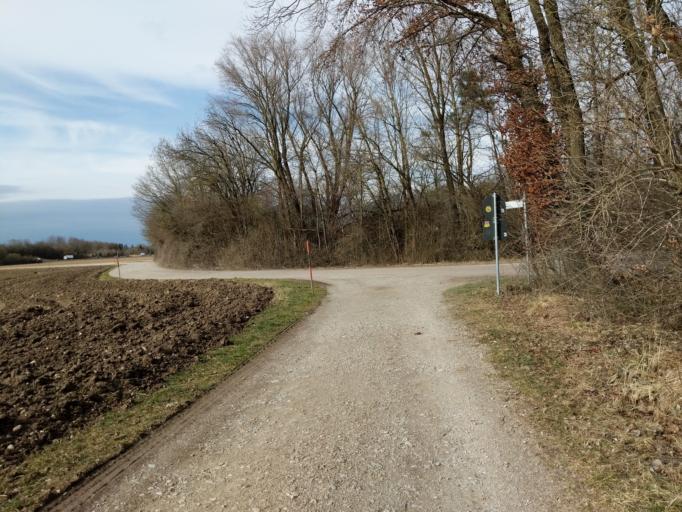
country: DE
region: Bavaria
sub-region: Upper Bavaria
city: Zorneding
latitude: 48.1021
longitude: 11.8356
